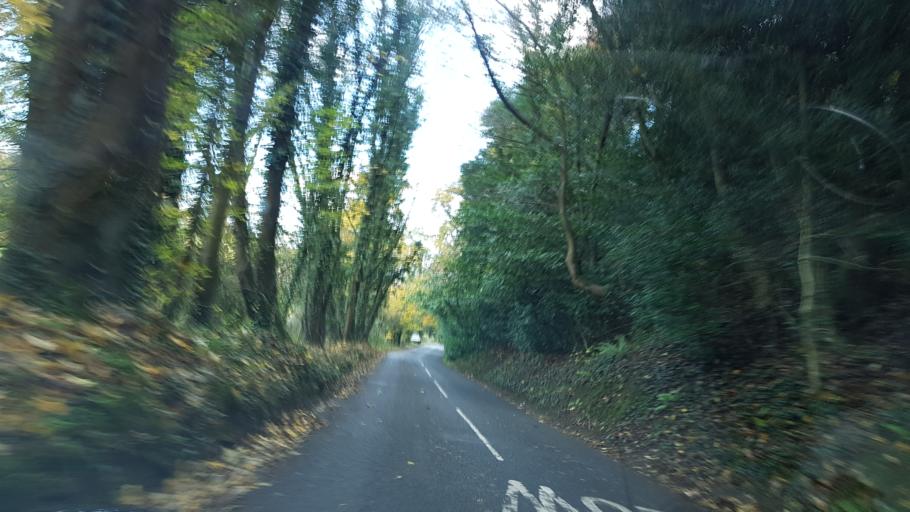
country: GB
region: England
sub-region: Surrey
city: Seale
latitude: 51.2223
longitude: -0.7164
